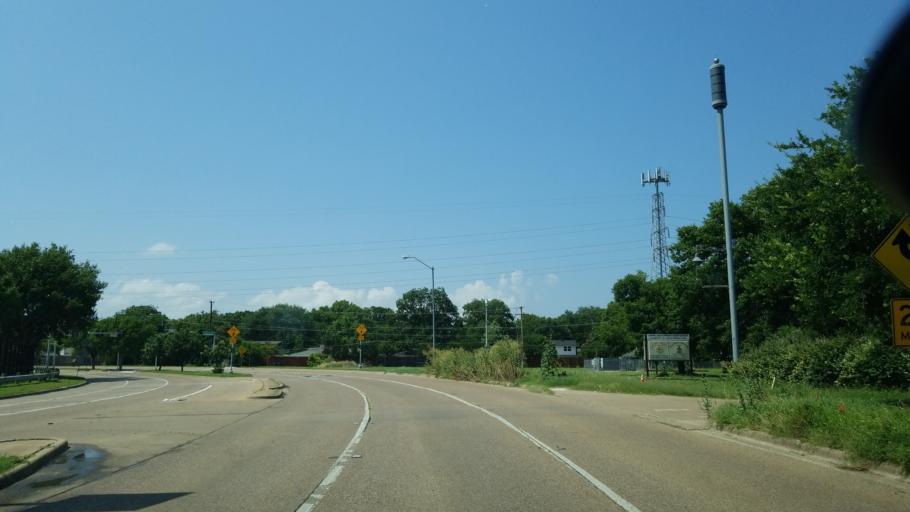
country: US
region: Texas
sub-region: Dallas County
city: Farmers Branch
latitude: 32.8844
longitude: -96.8657
